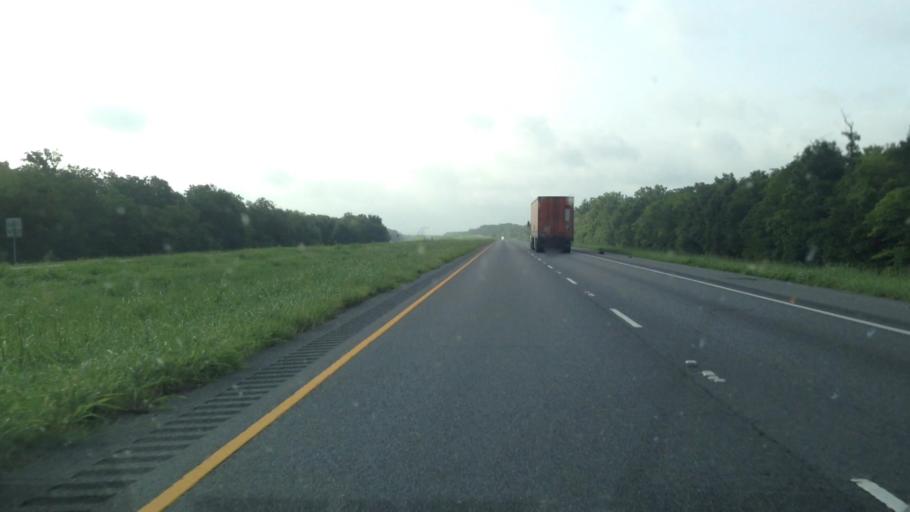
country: US
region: Louisiana
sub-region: Evangeline Parish
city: Ville Platte
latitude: 30.7322
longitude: -92.1304
